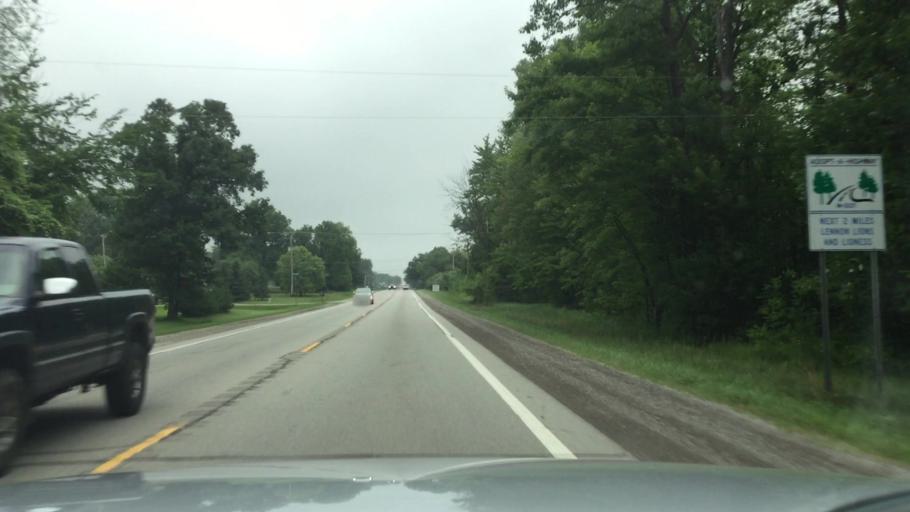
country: US
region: Michigan
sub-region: Shiawassee County
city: Durand
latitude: 42.9717
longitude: -83.9287
